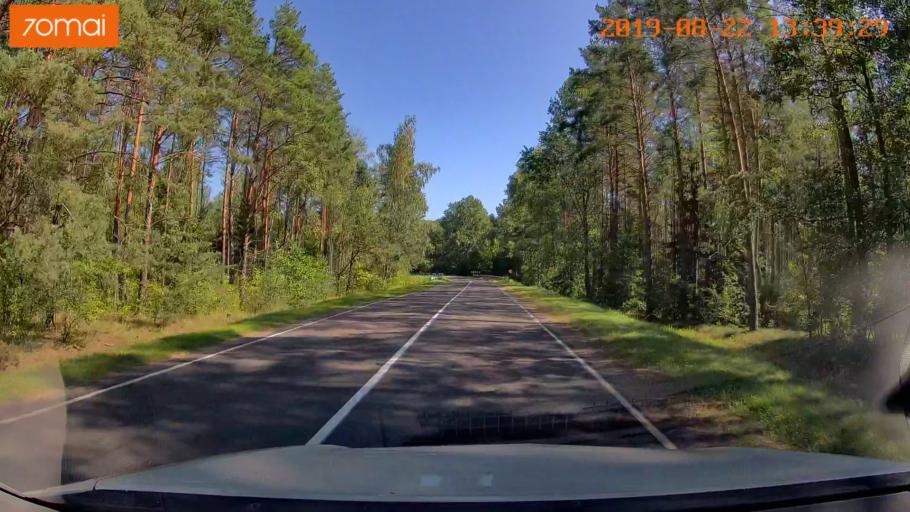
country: BY
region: Minsk
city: Staryya Darohi
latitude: 53.2274
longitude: 28.3508
